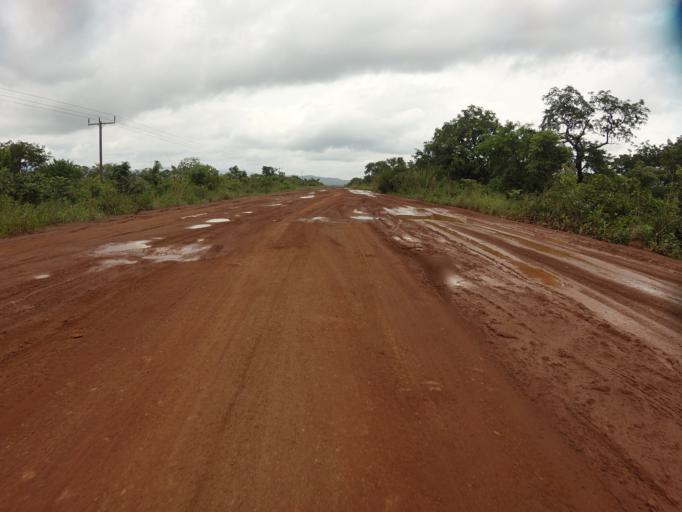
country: GH
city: Kpandae
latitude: 8.3076
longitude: 0.4843
